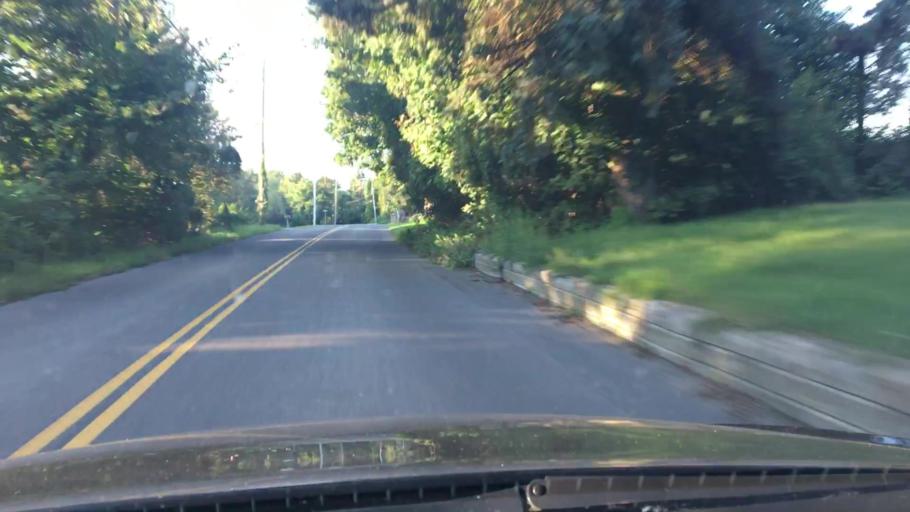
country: US
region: Connecticut
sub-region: Litchfield County
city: New Milford
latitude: 41.6116
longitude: -73.3722
